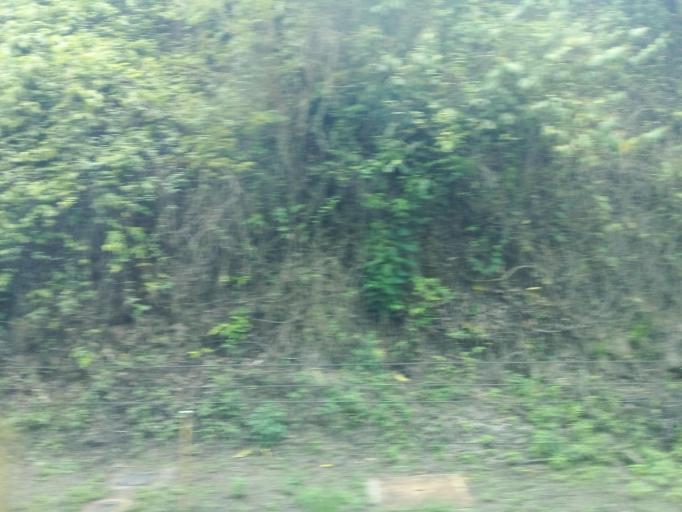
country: BR
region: Minas Gerais
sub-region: Nova Era
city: Nova Era
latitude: -19.7262
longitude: -42.9848
